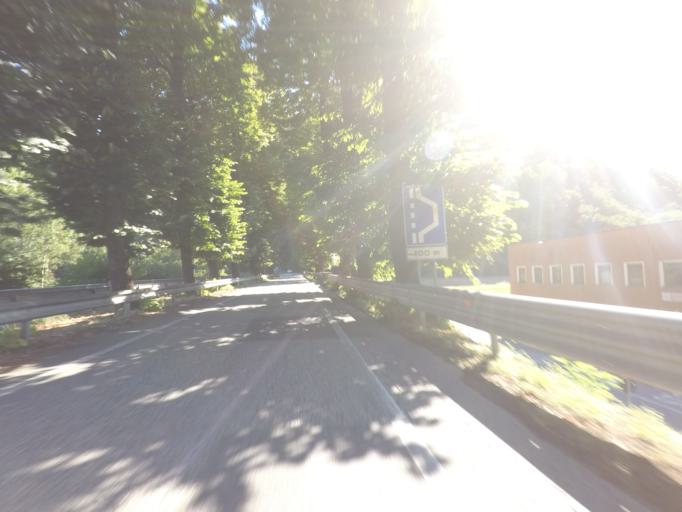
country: IT
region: Tuscany
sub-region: Provincia di Lucca
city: Valdottavo
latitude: 43.9407
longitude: 10.4951
